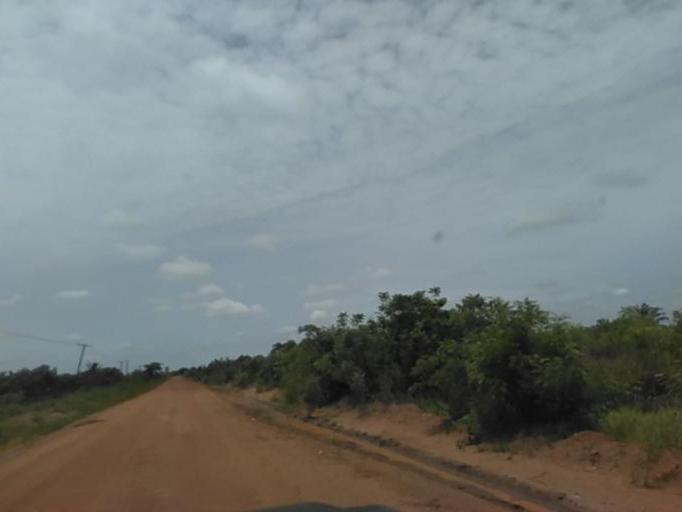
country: GH
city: Akropong
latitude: 6.0718
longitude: 0.2838
